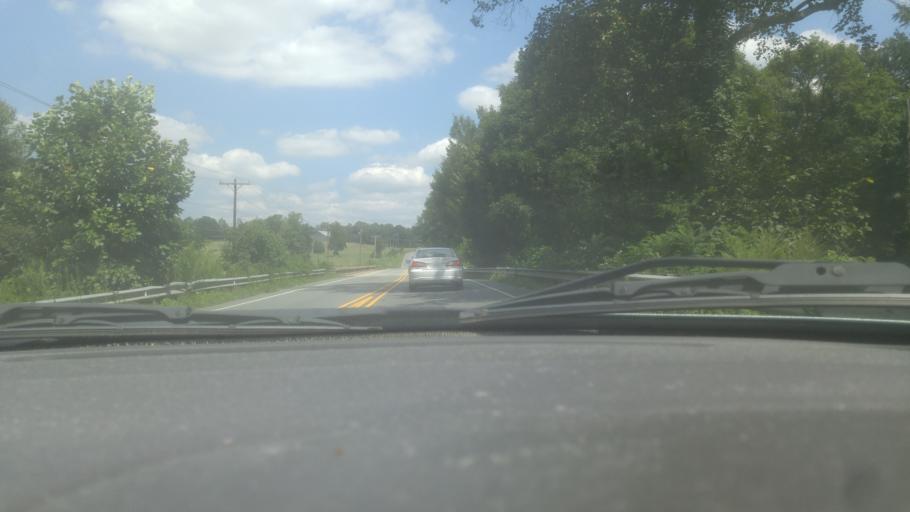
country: US
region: North Carolina
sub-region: Cabarrus County
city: Kannapolis
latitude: 35.4367
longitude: -80.6984
